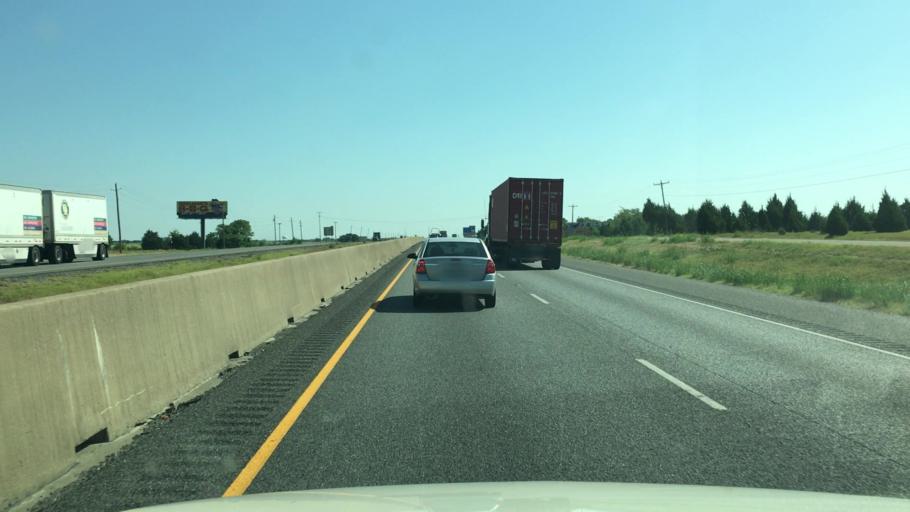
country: US
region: Texas
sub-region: Hunt County
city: Greenville
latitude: 33.0762
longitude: -96.1399
